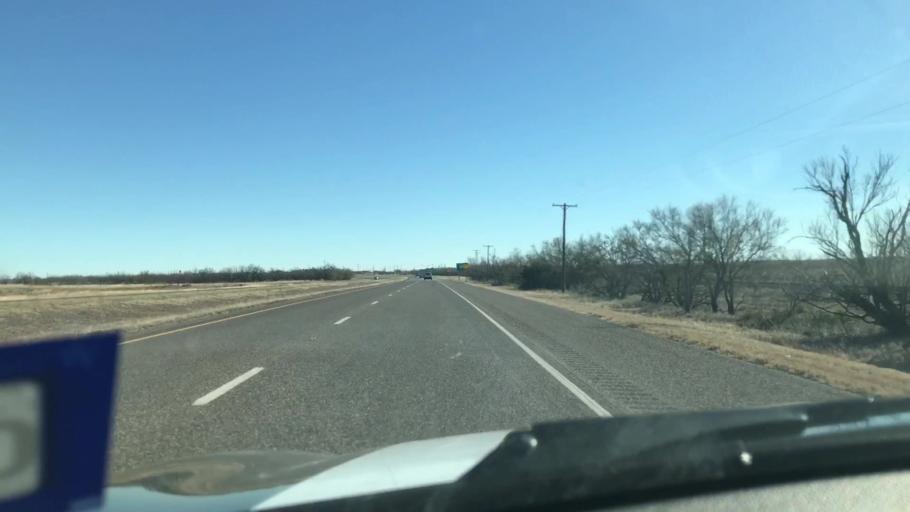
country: US
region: Texas
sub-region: Scurry County
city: Snyder
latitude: 32.8012
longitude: -100.9671
